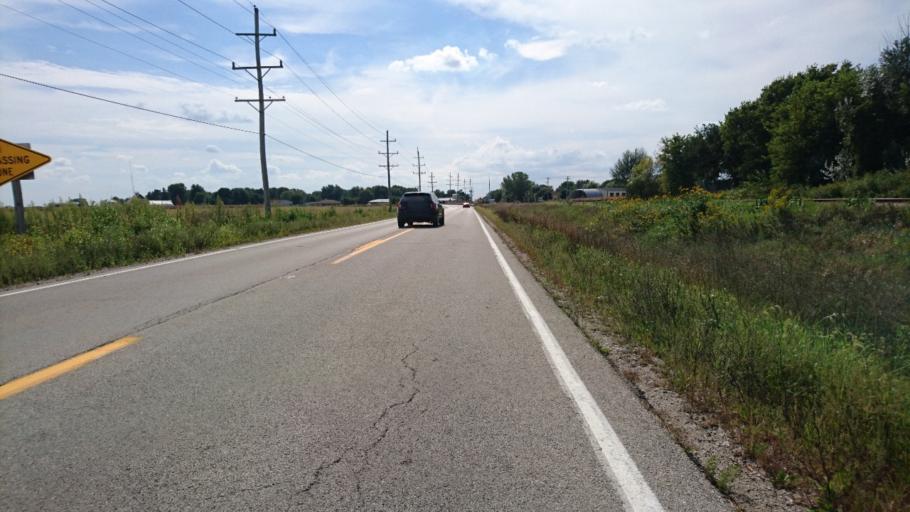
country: US
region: Illinois
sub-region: Grundy County
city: Gardner
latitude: 41.1948
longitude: -88.2991
